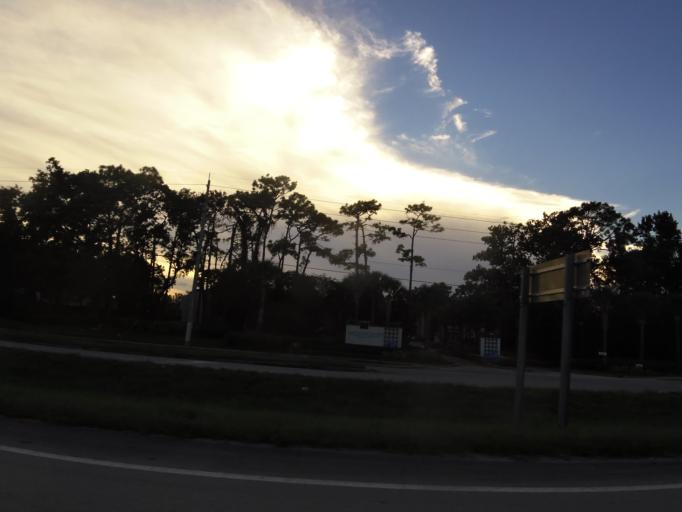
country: US
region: Florida
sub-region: Duval County
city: Jacksonville
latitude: 30.2292
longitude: -81.5521
